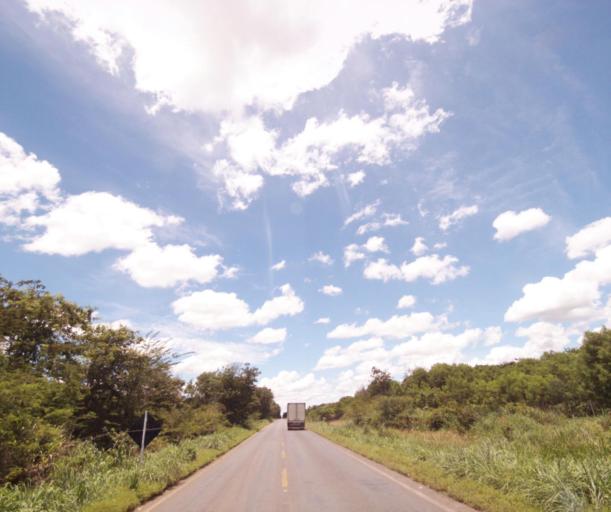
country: BR
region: Bahia
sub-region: Bom Jesus Da Lapa
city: Bom Jesus da Lapa
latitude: -13.2632
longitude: -43.5498
